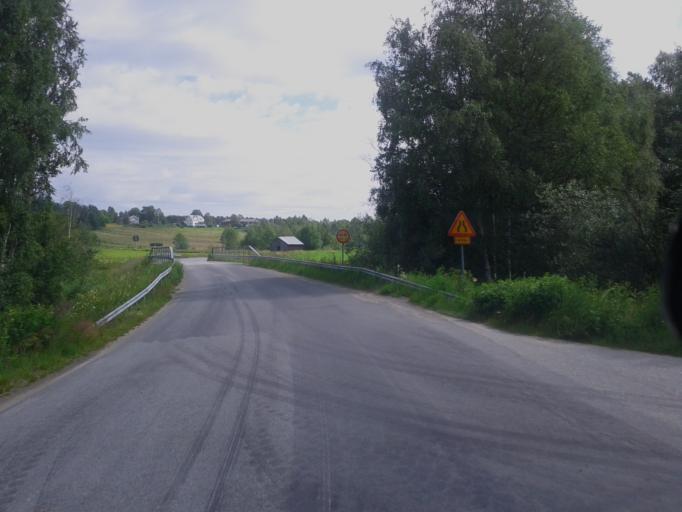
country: SE
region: Vaesternorrland
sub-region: OErnskoeldsviks Kommun
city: Ornskoldsvik
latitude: 63.2892
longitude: 18.8269
